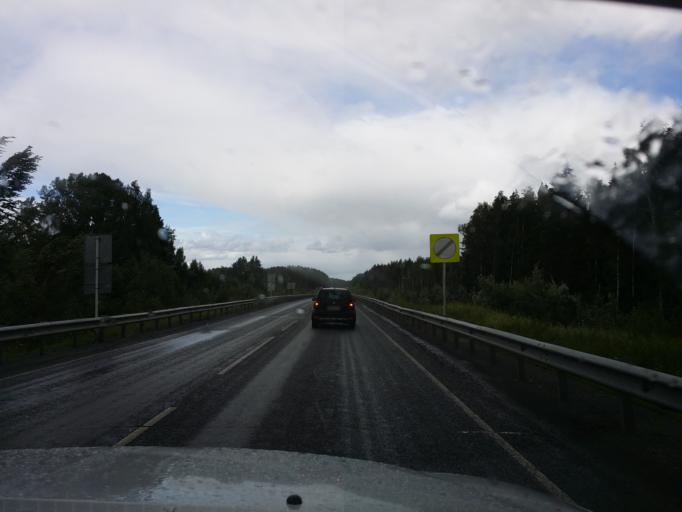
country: RU
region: Tjumen
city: Mendeleyevo
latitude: 58.4514
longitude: 68.4778
